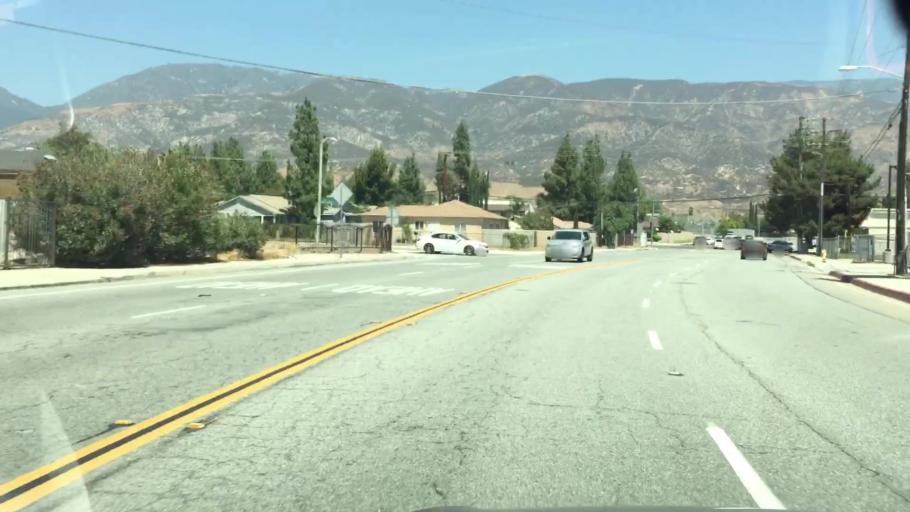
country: US
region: California
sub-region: San Bernardino County
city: Muscoy
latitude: 34.1678
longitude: -117.3173
